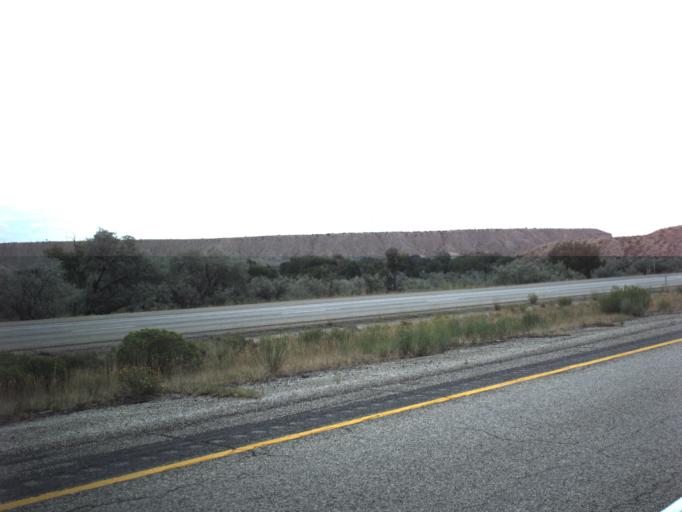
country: US
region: Utah
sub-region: Carbon County
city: Carbonville
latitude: 39.6142
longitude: -110.8387
